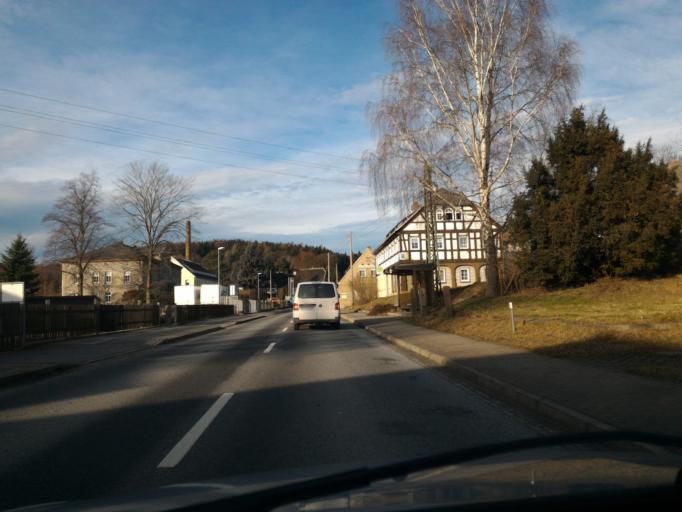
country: DE
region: Saxony
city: Steinigtwolmsdorf
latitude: 51.0545
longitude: 14.3756
